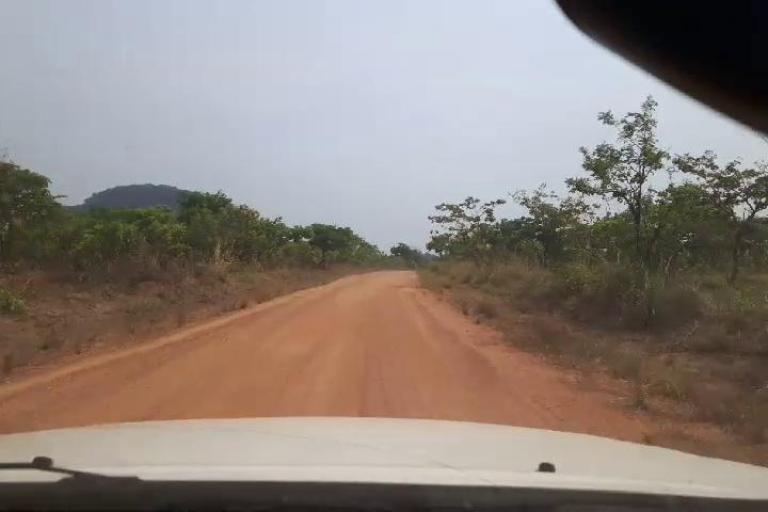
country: SL
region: Northern Province
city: Bumbuna
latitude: 8.8897
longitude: -11.8184
